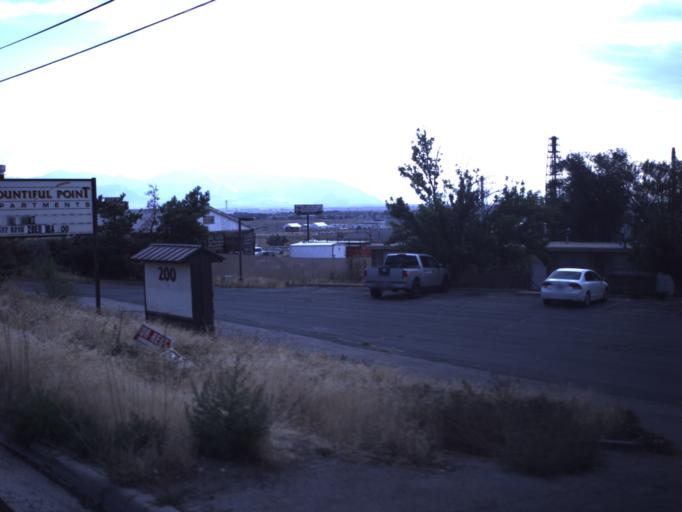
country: US
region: Utah
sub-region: Davis County
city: North Salt Lake
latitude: 40.8383
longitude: -111.9122
